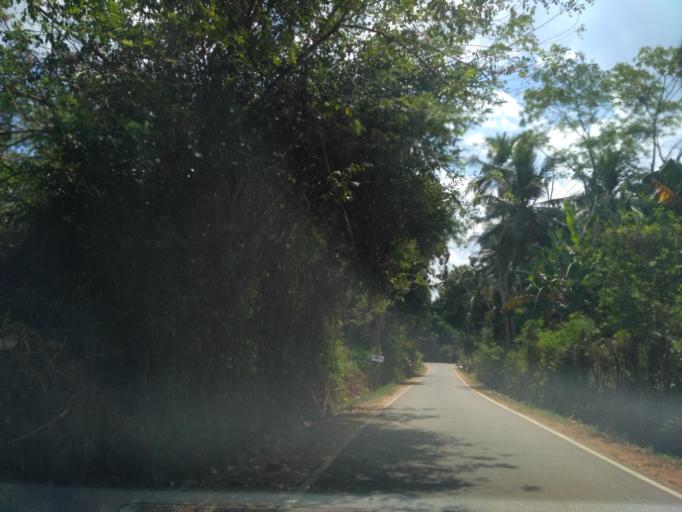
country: LK
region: North Western
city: Kuliyapitiya
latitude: 7.3277
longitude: 80.0626
